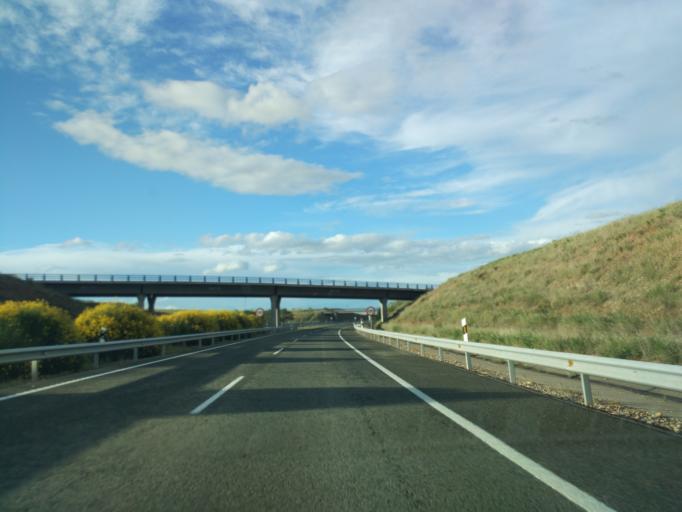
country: ES
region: Castille-La Mancha
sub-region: Provincia de Guadalajara
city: Marchamalo
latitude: 40.6716
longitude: -3.2160
